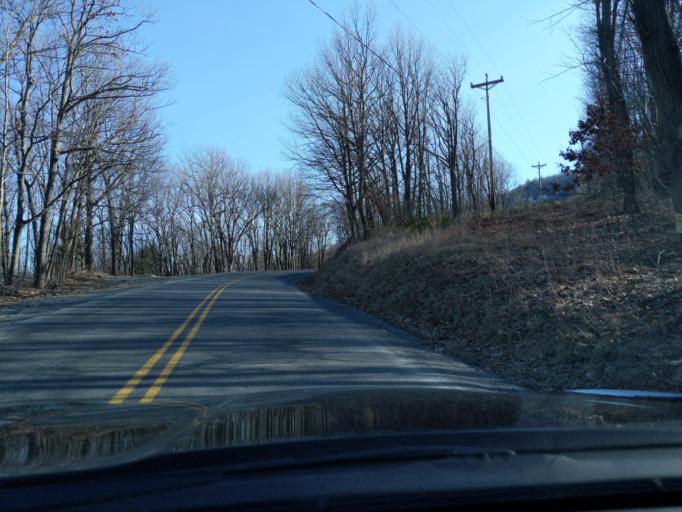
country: US
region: Pennsylvania
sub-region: Blair County
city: Hollidaysburg
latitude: 40.4054
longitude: -78.3070
